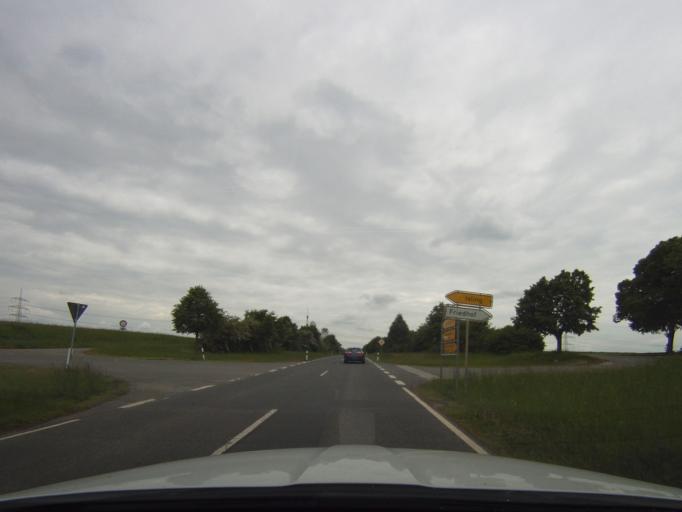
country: DE
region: Bavaria
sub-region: Upper Franconia
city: Altendorf
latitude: 50.1068
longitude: 11.1625
